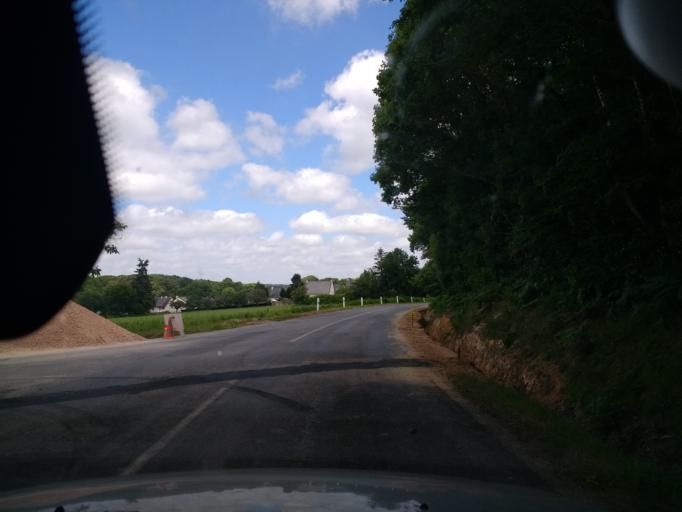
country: FR
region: Brittany
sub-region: Departement d'Ille-et-Vilaine
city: Paimpont
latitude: 48.0121
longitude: -2.1680
